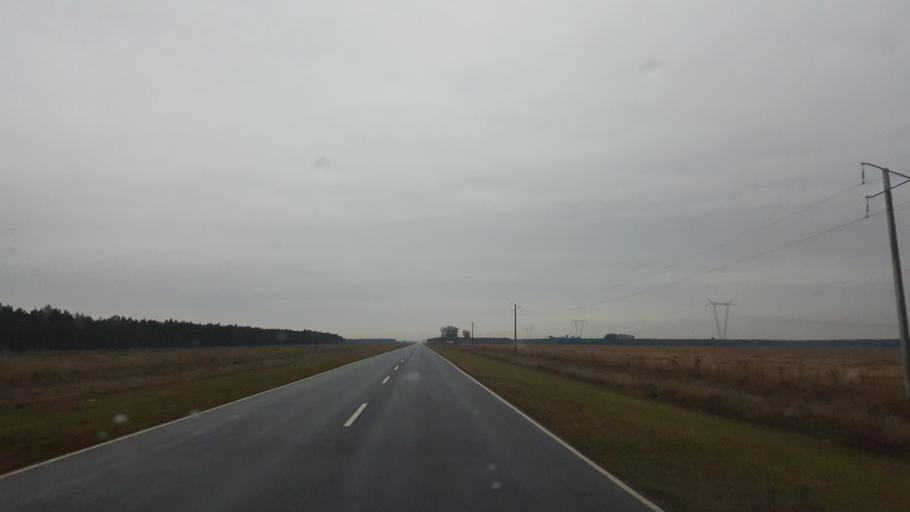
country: PY
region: Itapua
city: San Cosme y Damian
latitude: -27.5703
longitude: -56.2700
